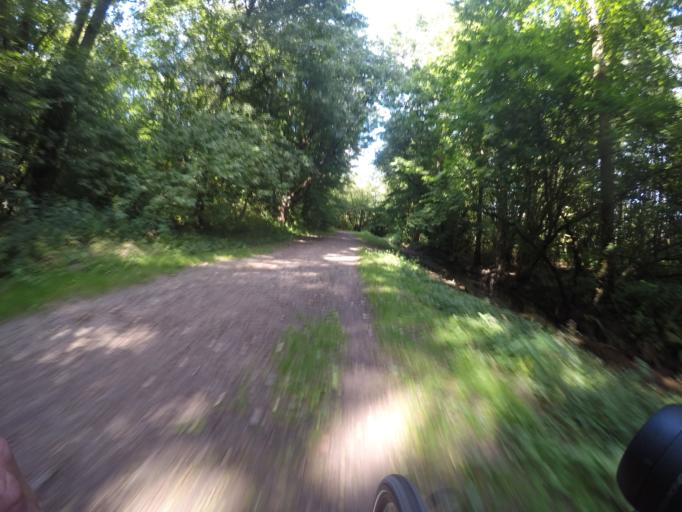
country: DE
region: Hamburg
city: Wandsbek
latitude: 53.5626
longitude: 10.1248
